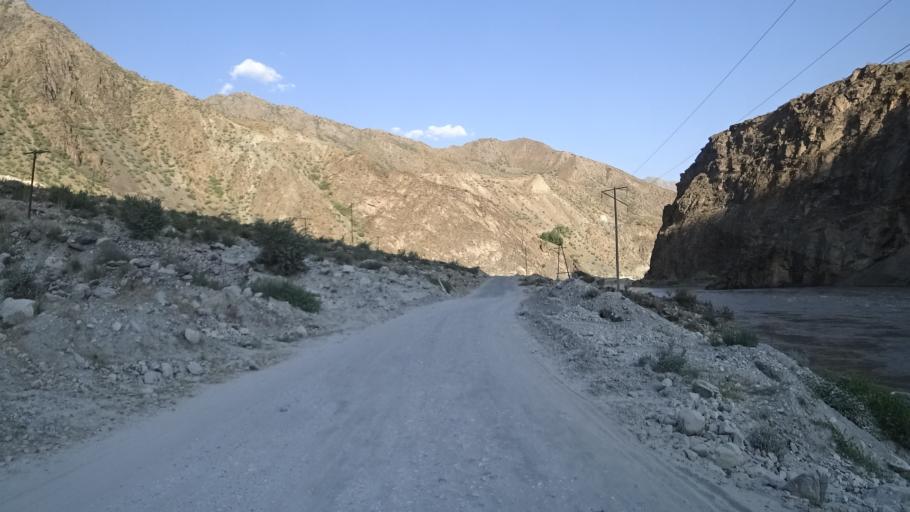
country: AF
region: Badakhshan
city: Maymay
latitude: 38.4902
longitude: 70.9929
